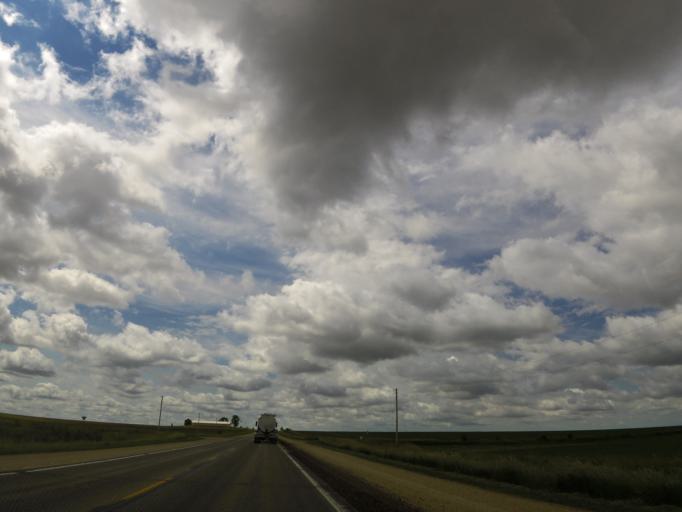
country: US
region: Iowa
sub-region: Howard County
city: Cresco
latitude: 43.3287
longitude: -92.2989
